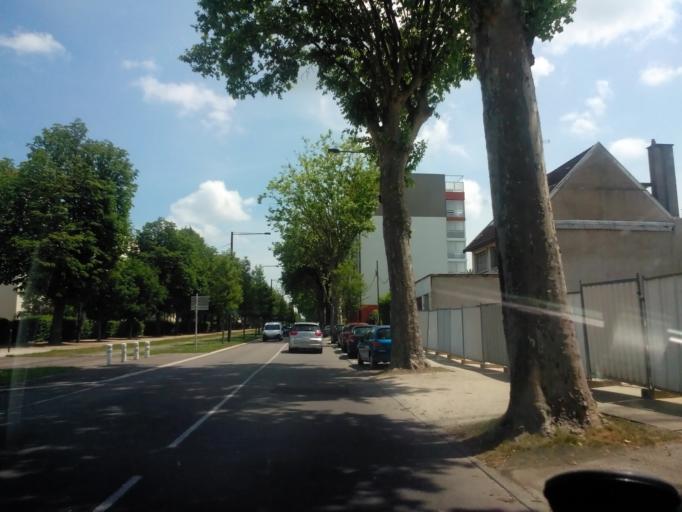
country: FR
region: Bourgogne
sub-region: Departement de la Cote-d'Or
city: Saint-Apollinaire
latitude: 47.3287
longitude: 5.0597
